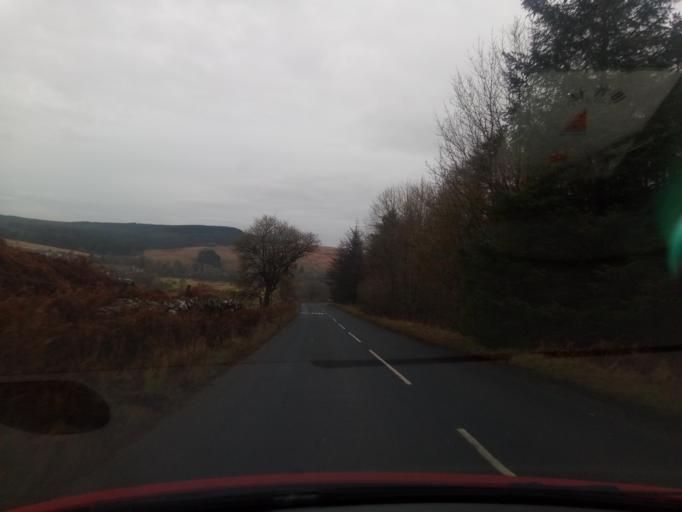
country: GB
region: England
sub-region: Northumberland
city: Haltwhistle
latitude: 55.1778
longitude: -2.4506
